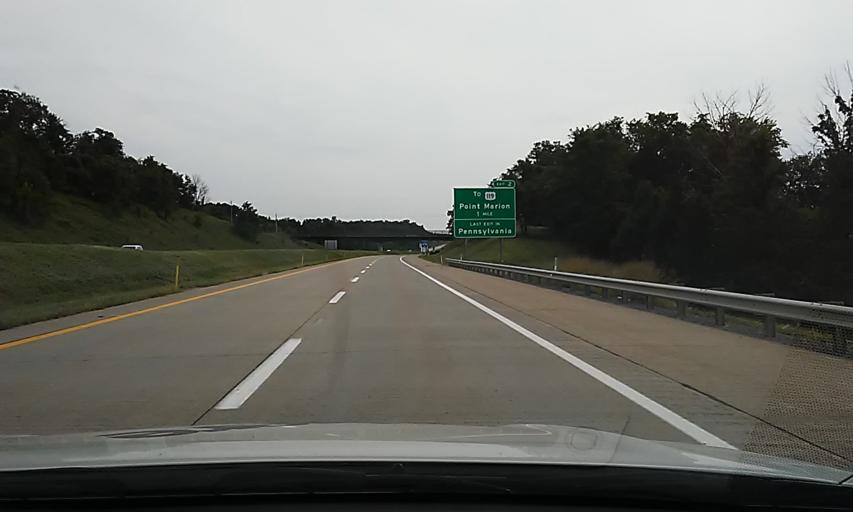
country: US
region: Pennsylvania
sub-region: Fayette County
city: Fairchance
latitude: 39.7573
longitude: -79.8001
